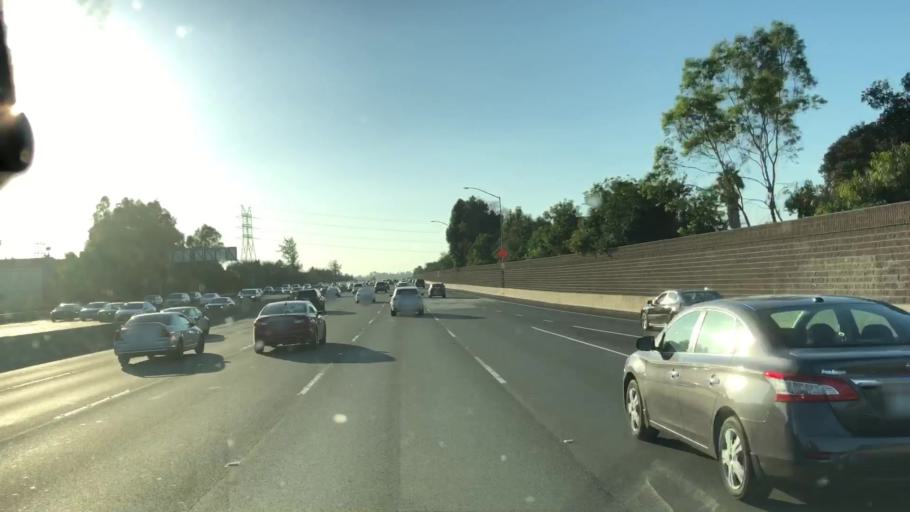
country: US
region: California
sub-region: Los Angeles County
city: Northridge
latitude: 34.1726
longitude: -118.5390
